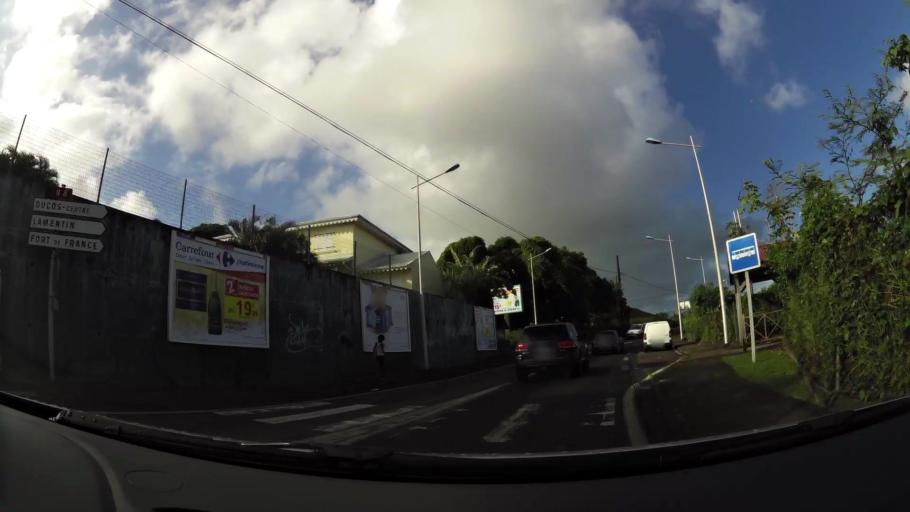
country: MQ
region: Martinique
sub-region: Martinique
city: Ducos
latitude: 14.5747
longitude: -60.9650
